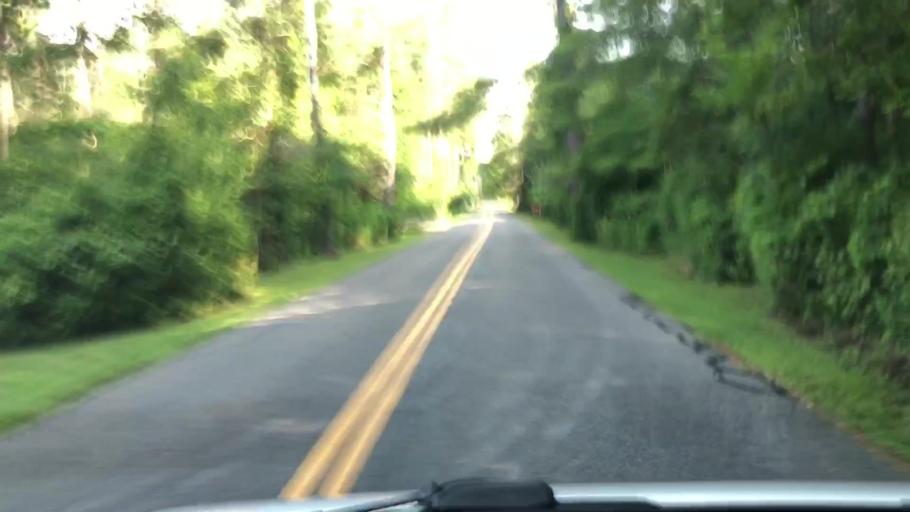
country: US
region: Massachusetts
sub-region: Berkshire County
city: Lee
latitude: 42.3053
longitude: -73.2627
